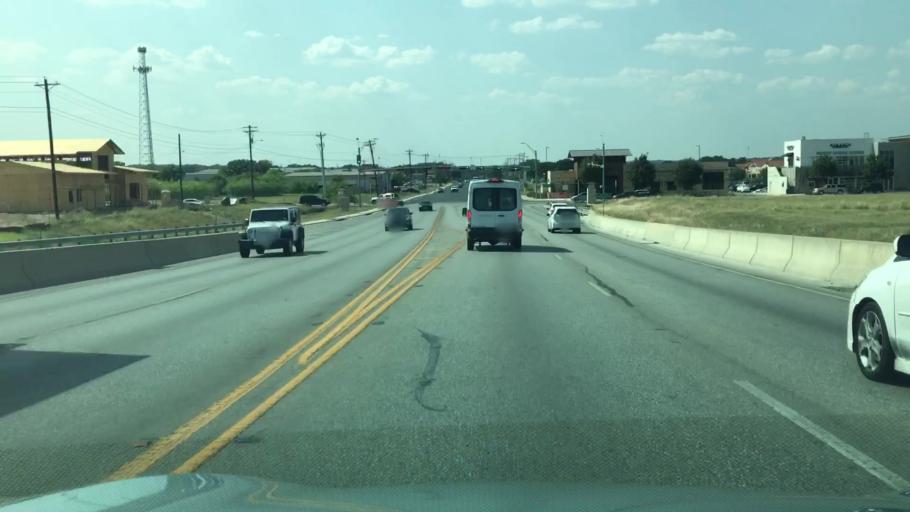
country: US
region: Texas
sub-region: Hays County
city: San Marcos
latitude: 29.8612
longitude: -97.9580
